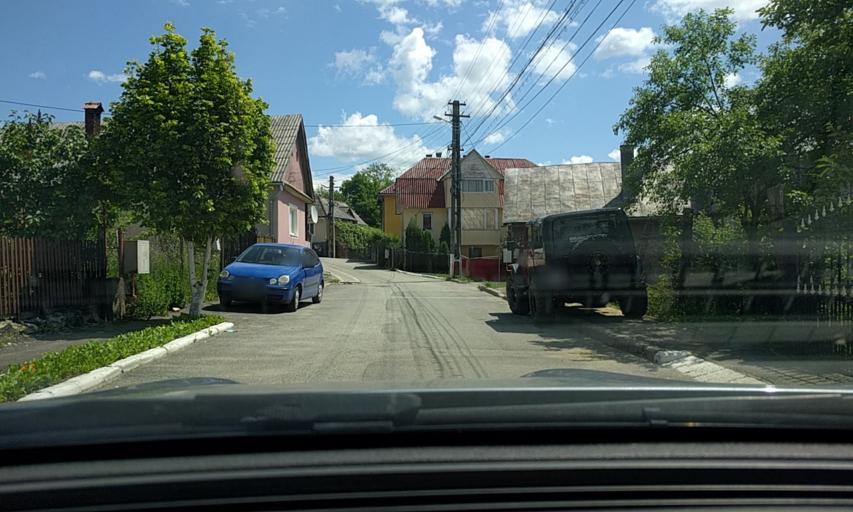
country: RO
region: Bistrita-Nasaud
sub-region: Oras Nasaud
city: Nasaud
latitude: 47.2897
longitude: 24.3939
